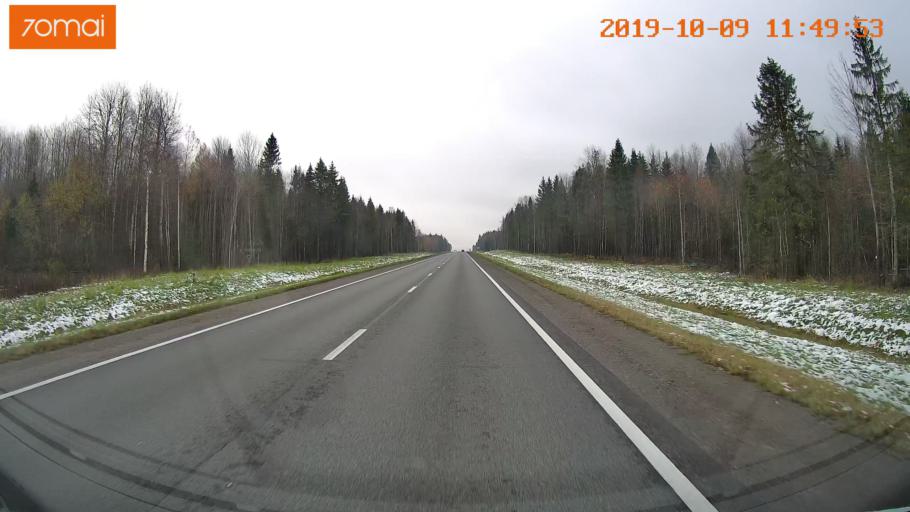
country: RU
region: Vologda
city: Gryazovets
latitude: 58.8126
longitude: 40.2375
